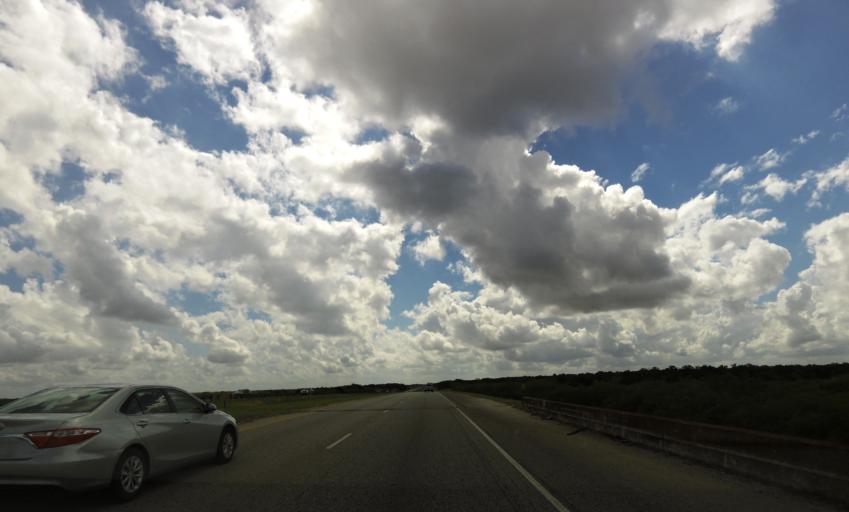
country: US
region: Texas
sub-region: Gonzales County
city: Gonzales
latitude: 29.6496
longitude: -97.4842
